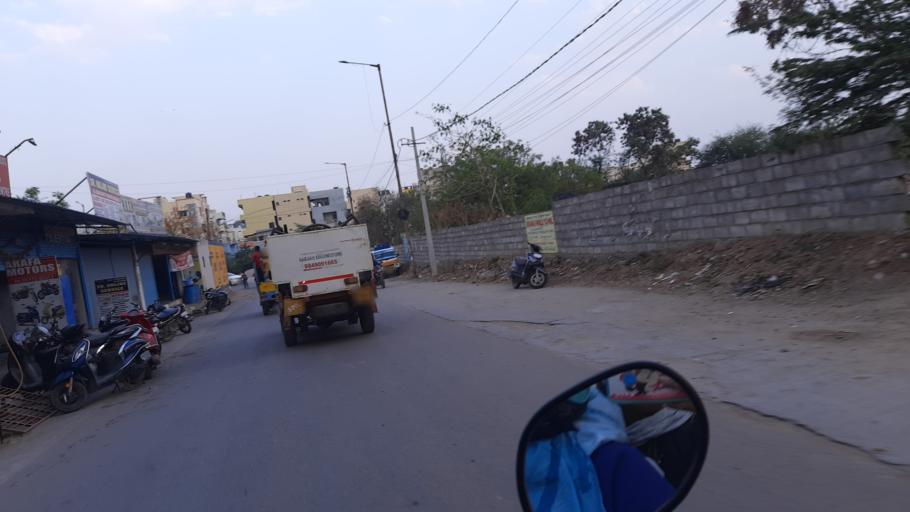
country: IN
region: Telangana
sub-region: Rangareddi
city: Kukatpalli
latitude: 17.4930
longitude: 78.4234
